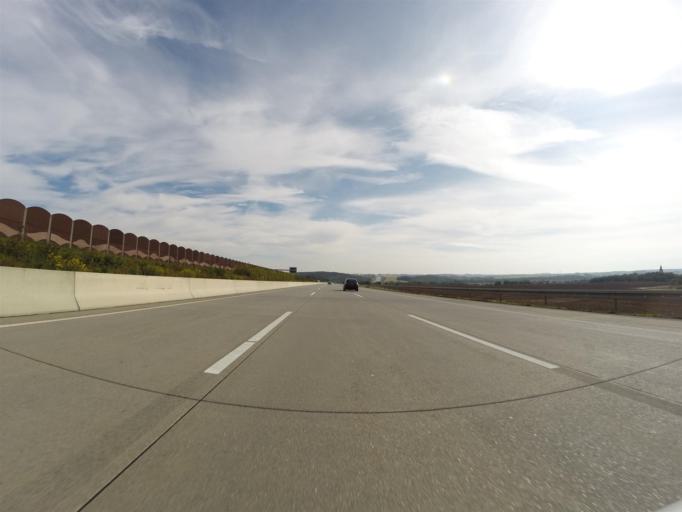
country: DE
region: Thuringia
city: Posterstein
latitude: 50.8705
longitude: 12.2472
